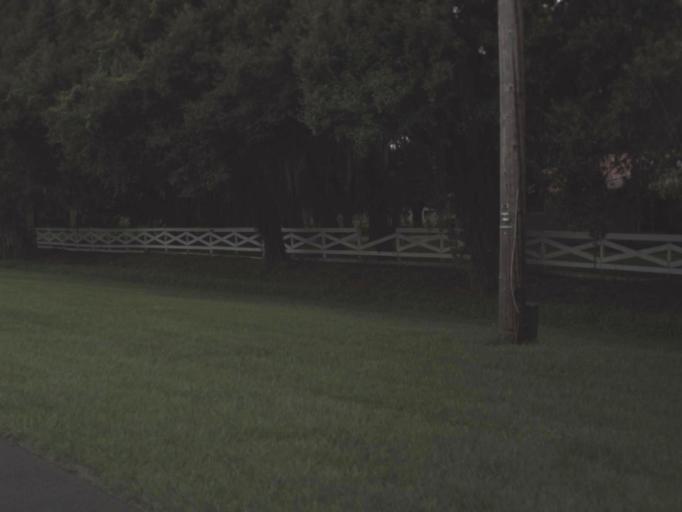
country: US
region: Florida
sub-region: Pasco County
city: Crystal Springs
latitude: 28.1309
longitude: -82.1483
